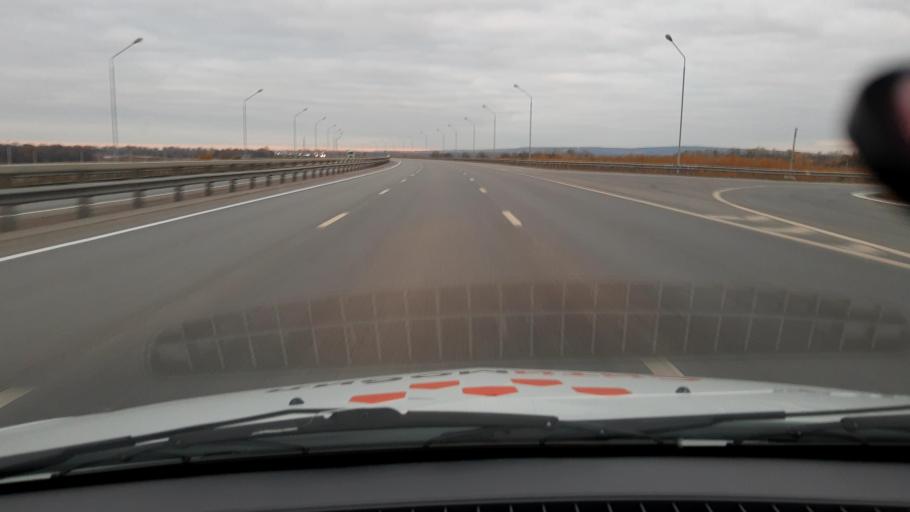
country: RU
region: Bashkortostan
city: Ufa
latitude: 54.6425
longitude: 55.9450
